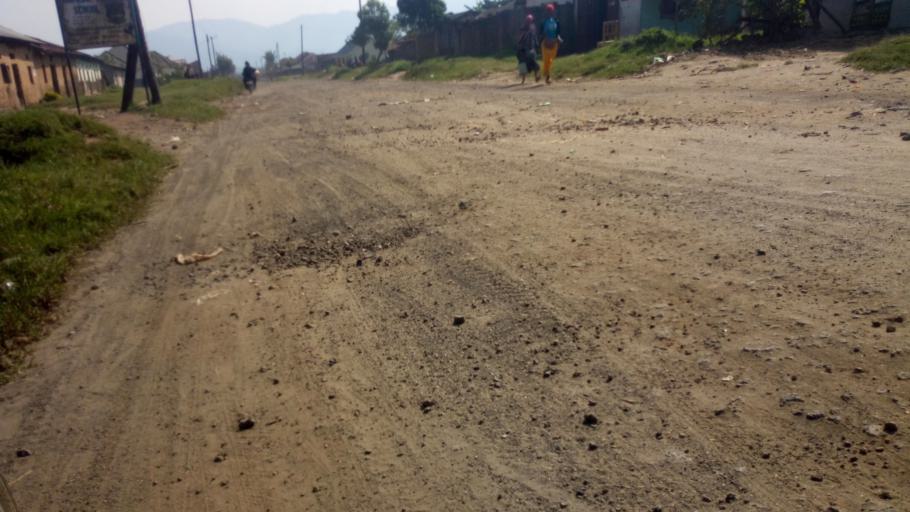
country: UG
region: Western Region
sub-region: Kisoro District
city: Kisoro
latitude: -1.2470
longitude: 29.7132
